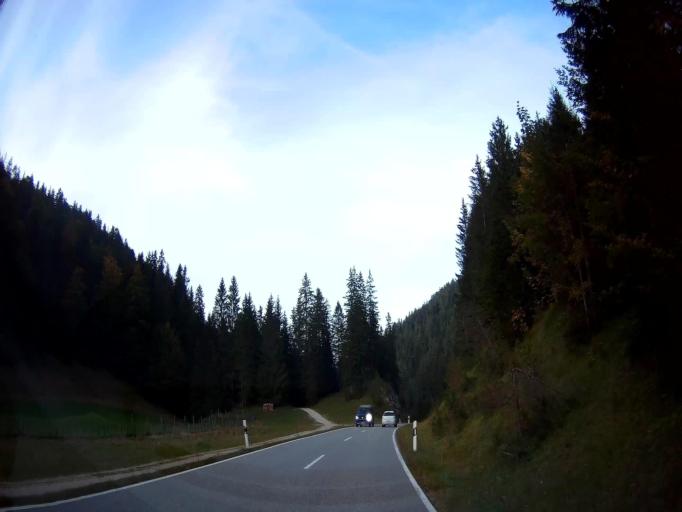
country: DE
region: Bavaria
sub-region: Upper Bavaria
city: Ramsau
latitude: 47.6289
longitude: 12.9069
